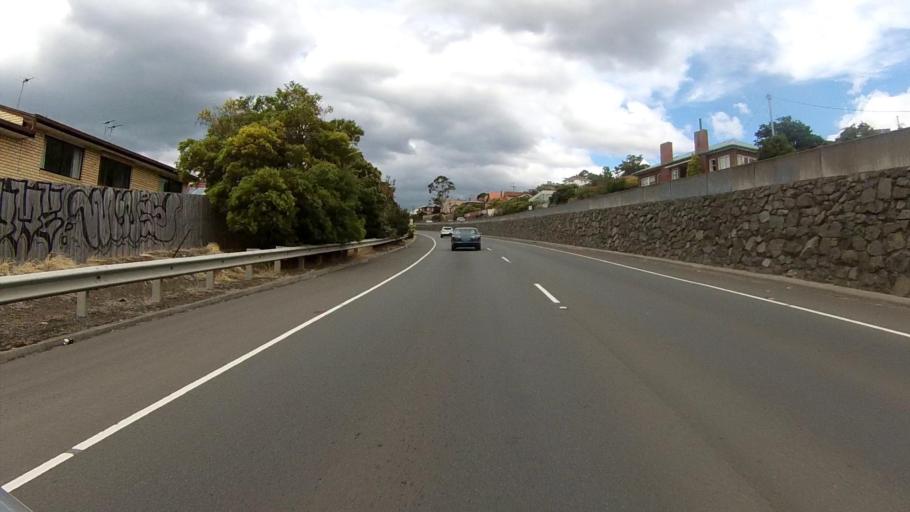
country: AU
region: Tasmania
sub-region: Hobart
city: Dynnyrne
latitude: -42.9004
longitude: 147.3156
